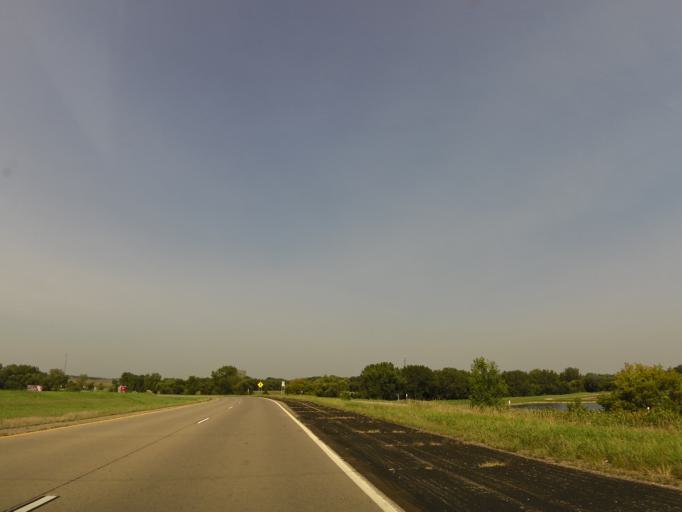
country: US
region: Minnesota
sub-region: Carver County
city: Cologne
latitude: 44.7682
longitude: -93.7909
